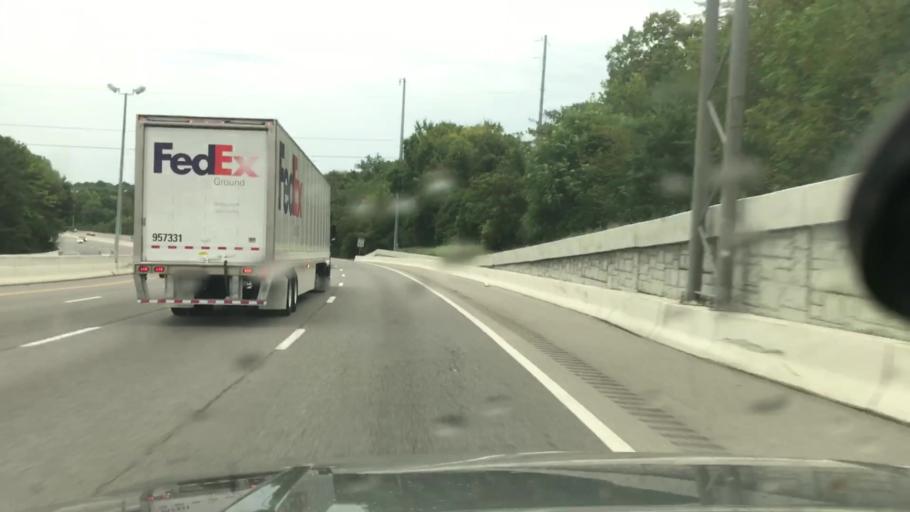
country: US
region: Tennessee
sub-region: Davidson County
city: Lakewood
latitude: 36.2036
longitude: -86.6818
